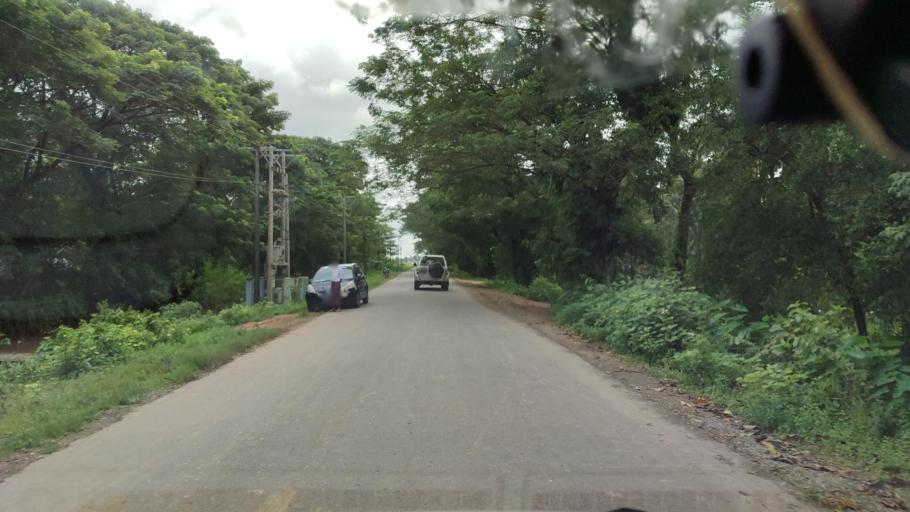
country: MM
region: Bago
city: Thanatpin
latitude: 17.1035
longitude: 96.5193
